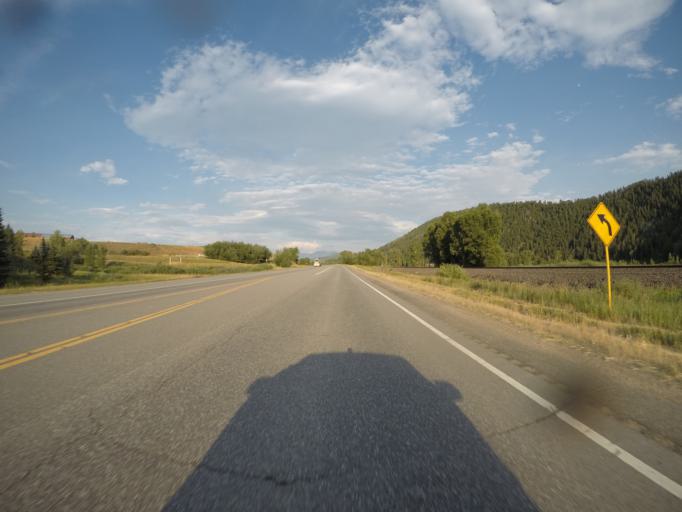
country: US
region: Colorado
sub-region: Routt County
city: Steamboat Springs
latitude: 40.4844
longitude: -106.9835
